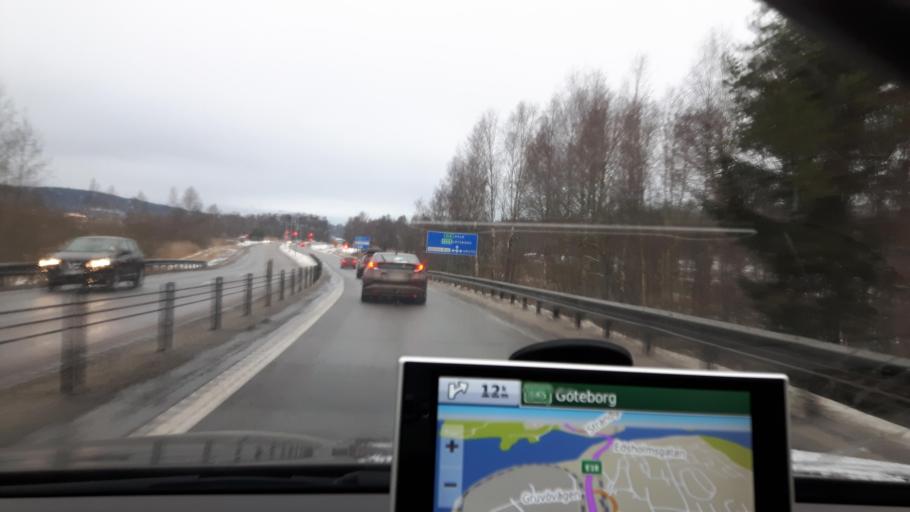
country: SE
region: Vaermland
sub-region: Grums Kommun
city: Grums
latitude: 59.3441
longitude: 13.1103
